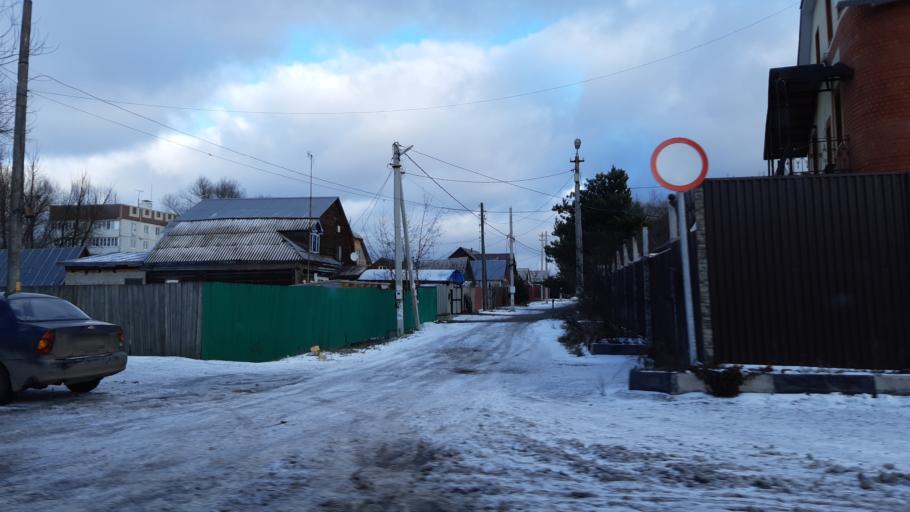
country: RU
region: Moskovskaya
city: Noginsk-9
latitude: 55.9506
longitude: 38.5527
